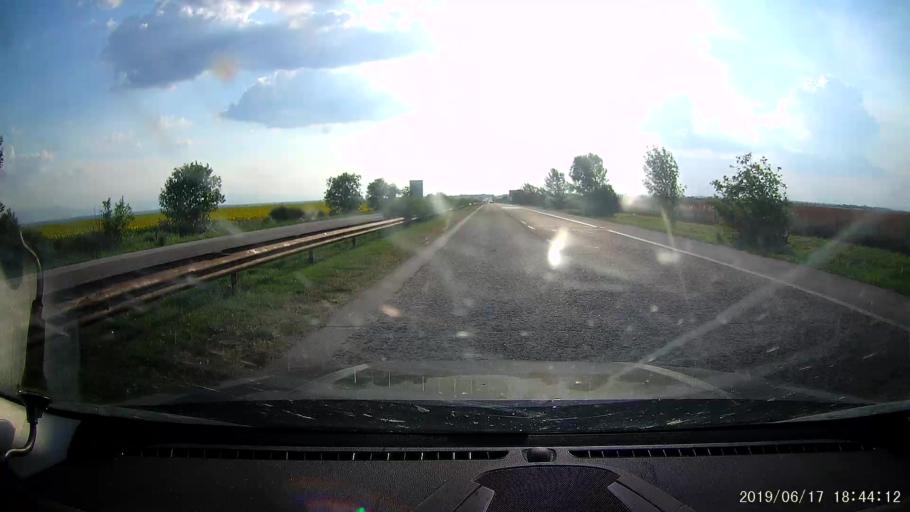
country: BG
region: Stara Zagora
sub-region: Obshtina Chirpan
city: Chirpan
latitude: 42.1925
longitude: 25.1897
